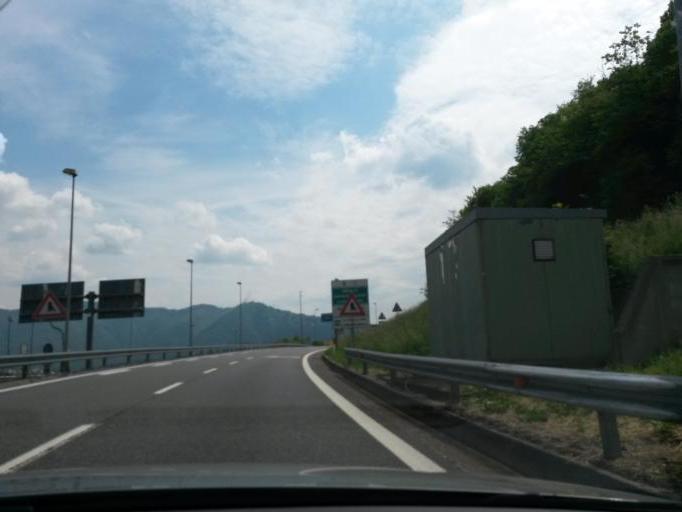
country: IT
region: Lombardy
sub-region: Provincia di Como
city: Maslianico
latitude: 45.8410
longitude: 9.0419
